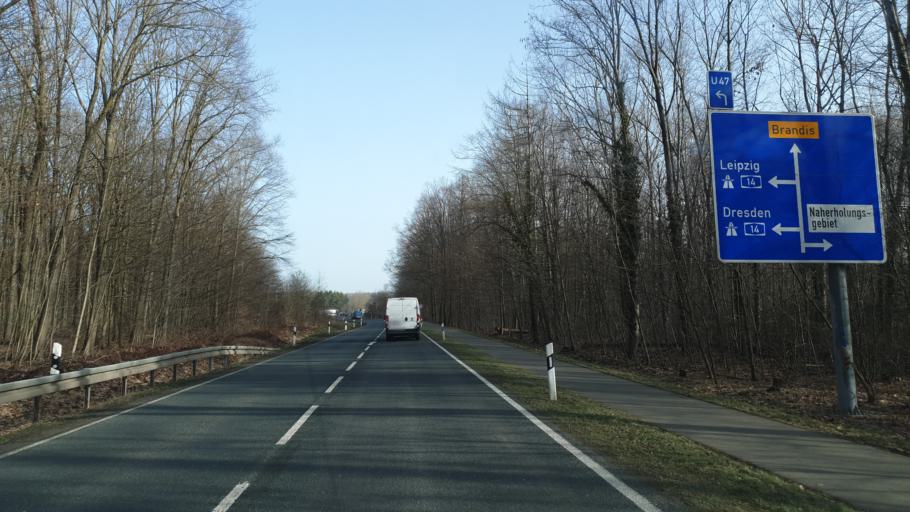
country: DE
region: Saxony
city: Naunhof
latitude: 51.2995
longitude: 12.5968
